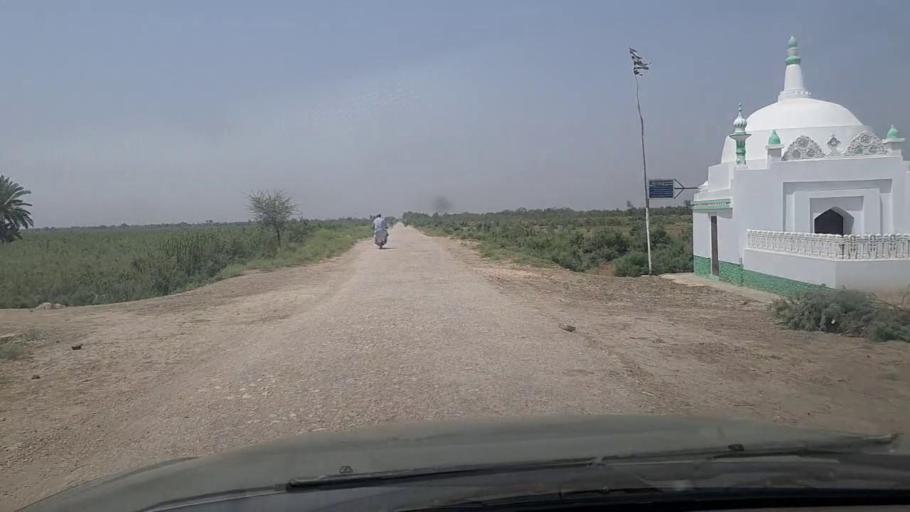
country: PK
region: Sindh
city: Adilpur
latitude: 27.9372
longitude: 69.2898
